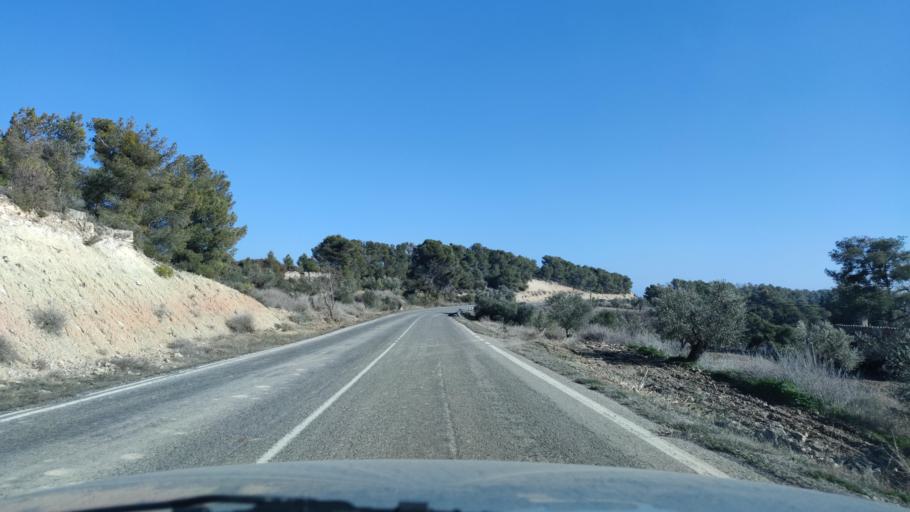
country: ES
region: Catalonia
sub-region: Provincia de Lleida
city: Maials
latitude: 41.3298
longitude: 0.4316
